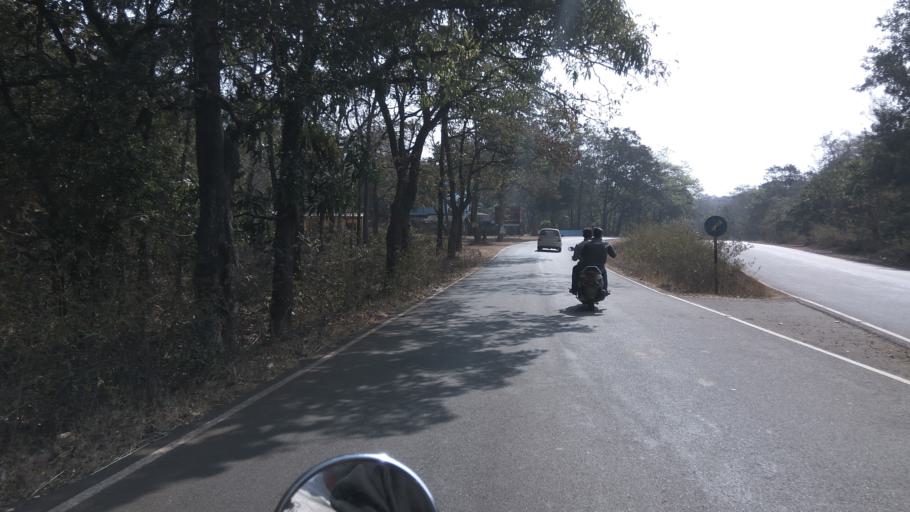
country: IN
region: Goa
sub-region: North Goa
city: Palle
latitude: 15.3797
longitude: 74.1459
